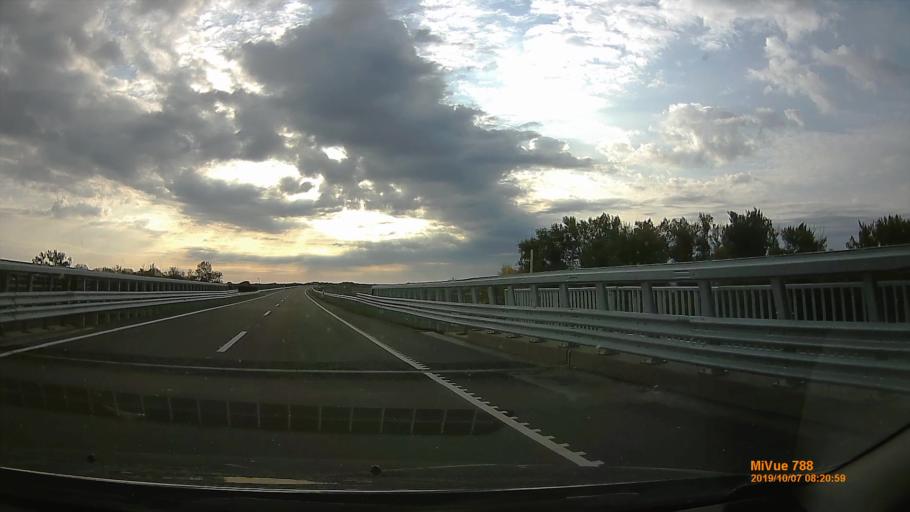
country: HU
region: Jasz-Nagykun-Szolnok
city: Kunszentmarton
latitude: 46.8640
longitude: 20.2907
